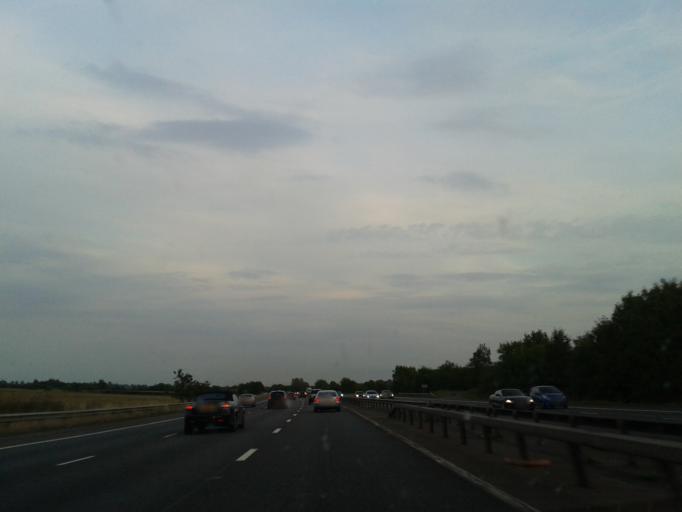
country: GB
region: England
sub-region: Oxfordshire
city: Hanwell
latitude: 52.1405
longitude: -1.4100
